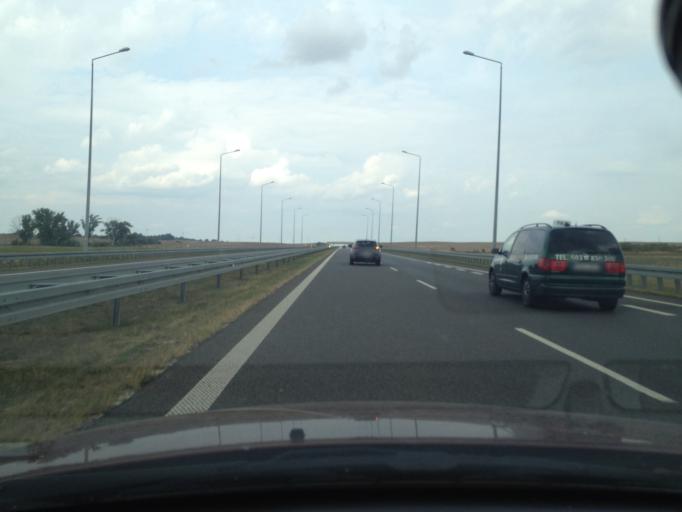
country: PL
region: West Pomeranian Voivodeship
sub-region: Powiat pyrzycki
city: Kozielice
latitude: 53.0561
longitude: 14.8648
